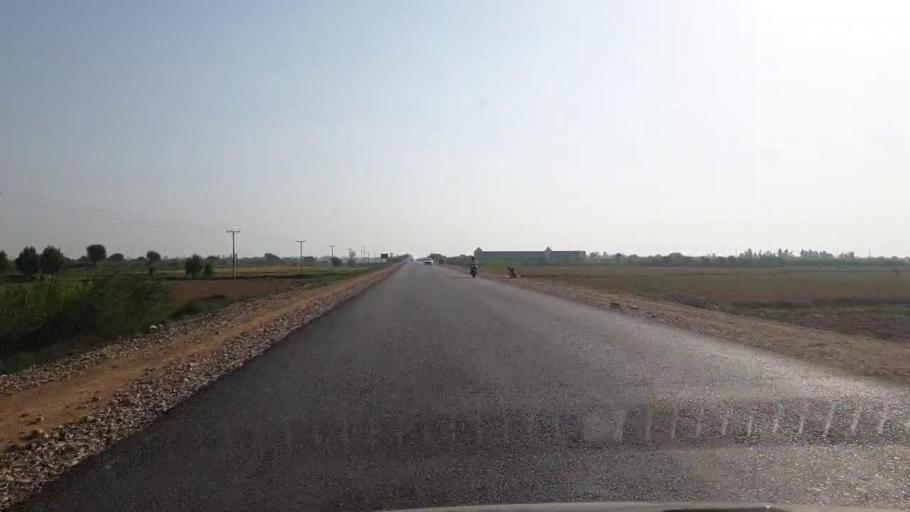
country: PK
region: Sindh
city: Badin
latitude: 24.6600
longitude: 68.8855
